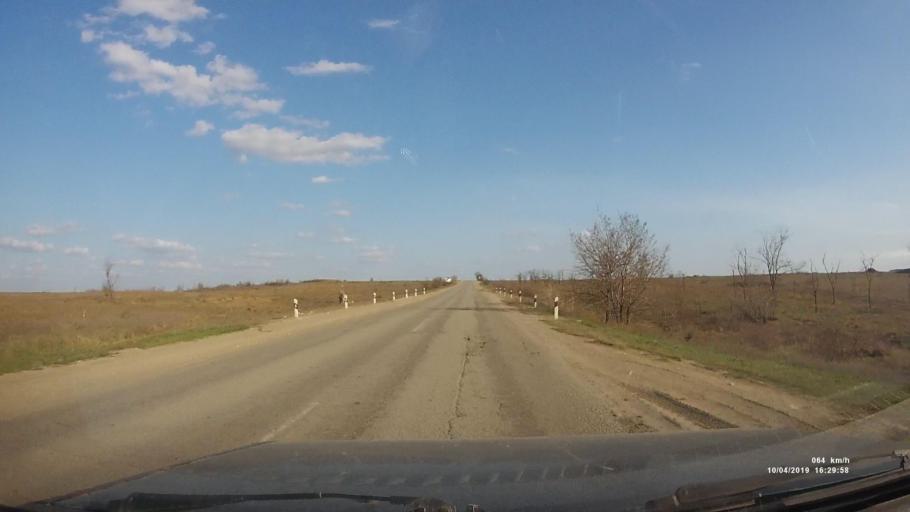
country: RU
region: Rostov
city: Staraya Stanitsa
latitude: 48.2652
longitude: 40.3611
